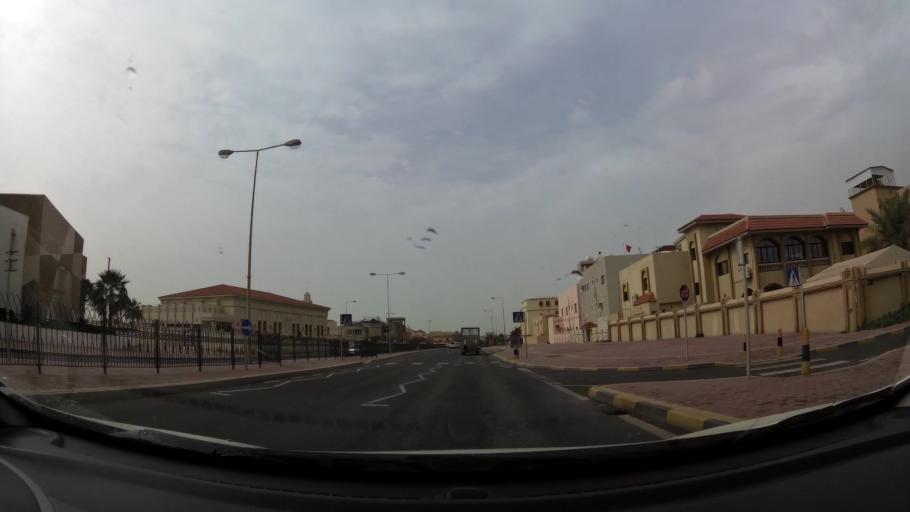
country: BH
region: Northern
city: Ar Rifa'
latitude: 26.1379
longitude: 50.5593
